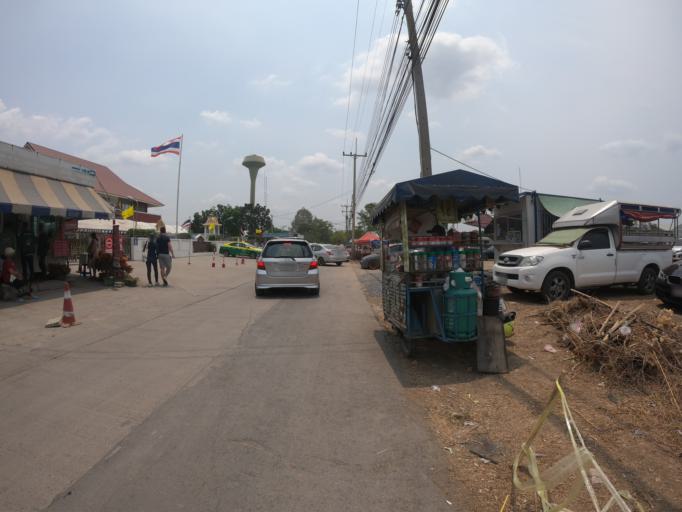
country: TH
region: Phra Nakhon Si Ayutthaya
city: Ban Bang Kadi Pathum Thani
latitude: 14.0081
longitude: 100.5689
